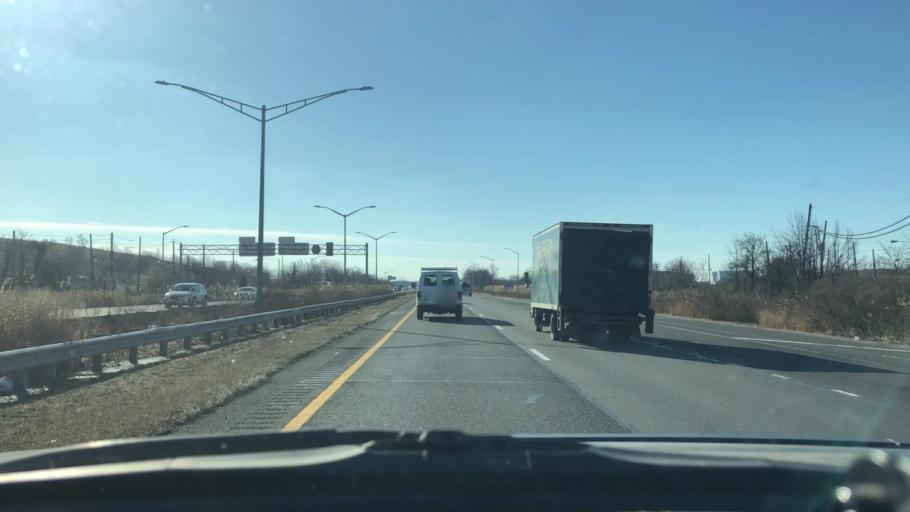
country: US
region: New York
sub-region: Richmond County
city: Bloomfield
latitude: 40.5864
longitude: -74.1928
